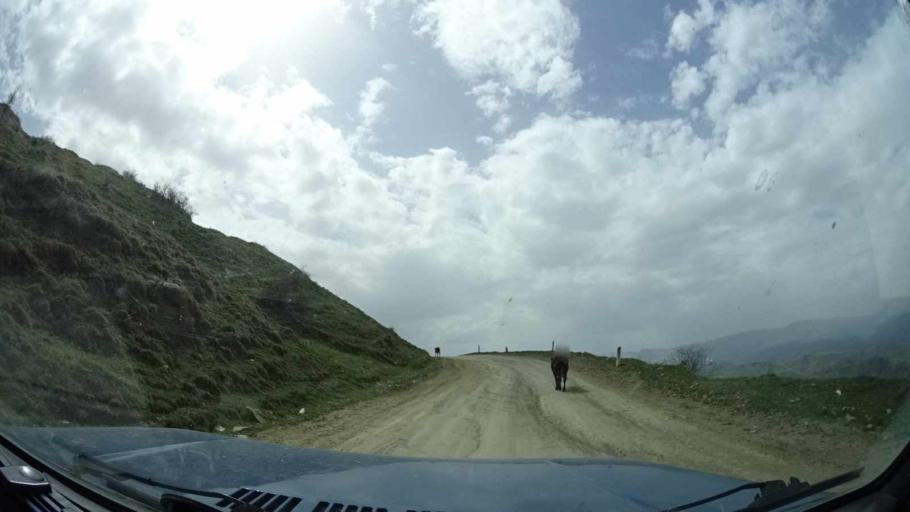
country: RU
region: Dagestan
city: Kubachi
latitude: 42.0894
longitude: 47.5827
